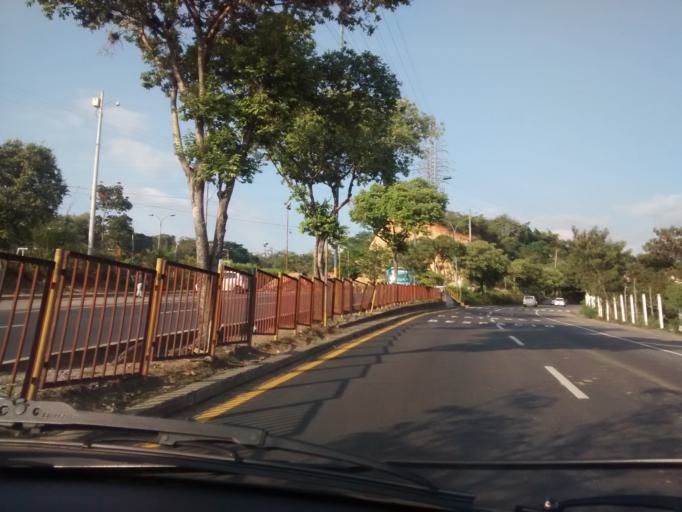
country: CO
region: Santander
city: Bucaramanga
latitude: 7.0933
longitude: -73.1301
